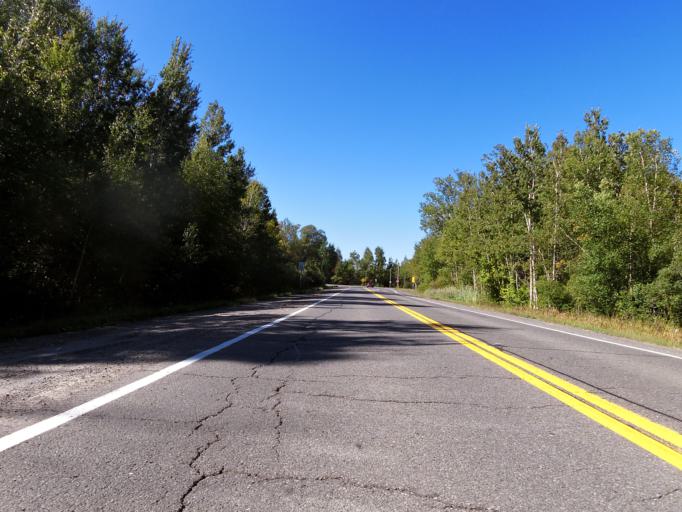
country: CA
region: Ontario
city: Clarence-Rockland
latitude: 45.3286
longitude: -75.4321
